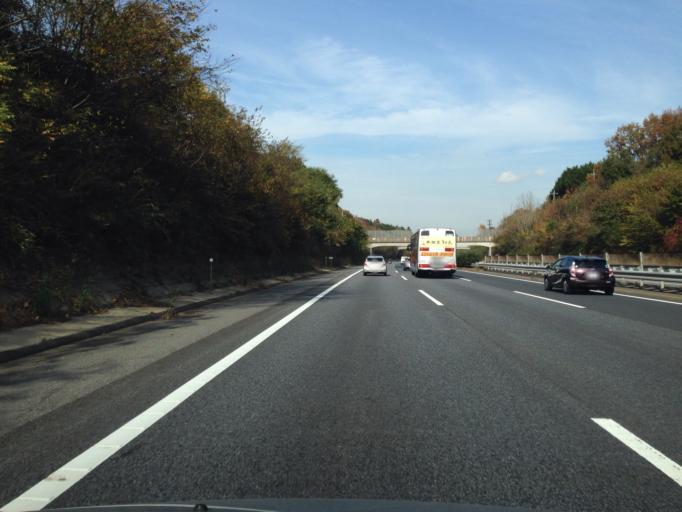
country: JP
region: Ibaraki
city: Naka
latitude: 36.0785
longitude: 140.1546
